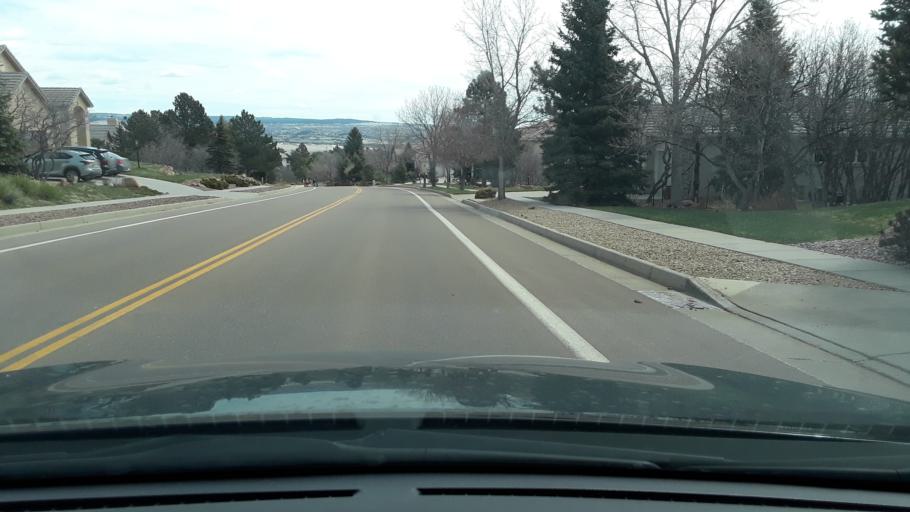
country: US
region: Colorado
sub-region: El Paso County
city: Air Force Academy
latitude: 38.9534
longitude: -104.8734
